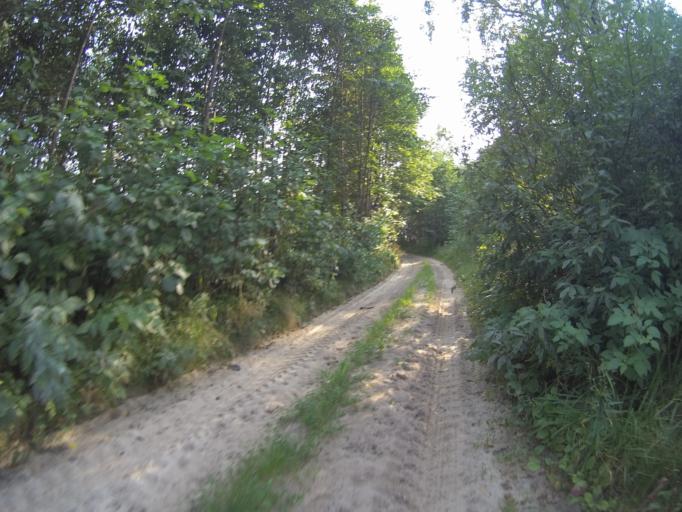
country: RU
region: Vladimir
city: Kommunar
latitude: 56.0479
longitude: 40.5622
